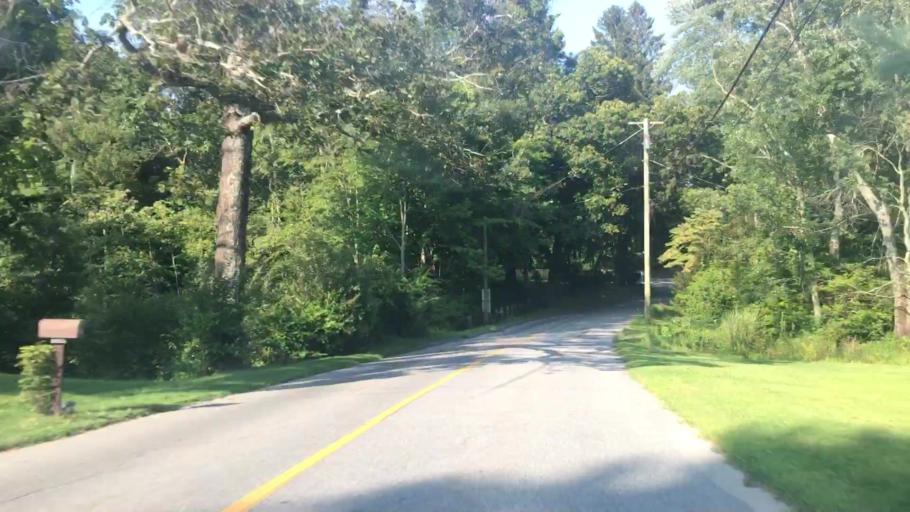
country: US
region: Connecticut
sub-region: Middlesex County
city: Deep River Center
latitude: 41.3850
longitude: -72.4476
